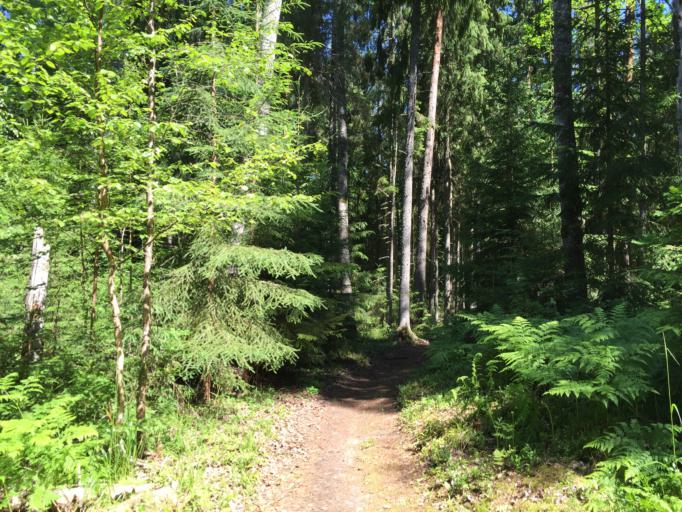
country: LV
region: Sigulda
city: Sigulda
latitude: 57.2238
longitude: 24.9102
